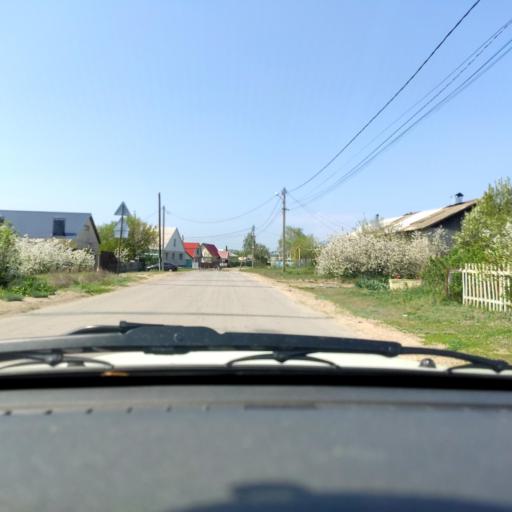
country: RU
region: Voronezj
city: Shilovo
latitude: 51.5551
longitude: 39.0707
